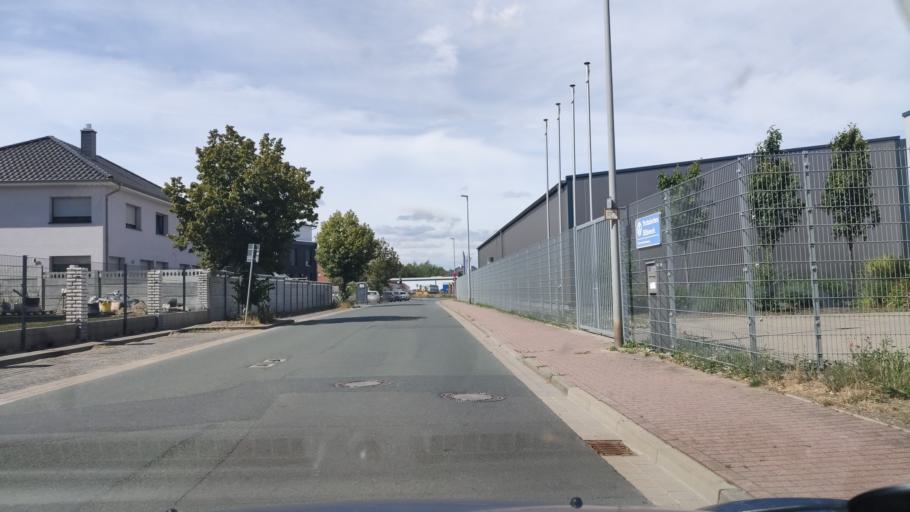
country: DE
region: Lower Saxony
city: Ronnenberg
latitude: 52.3438
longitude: 9.6538
